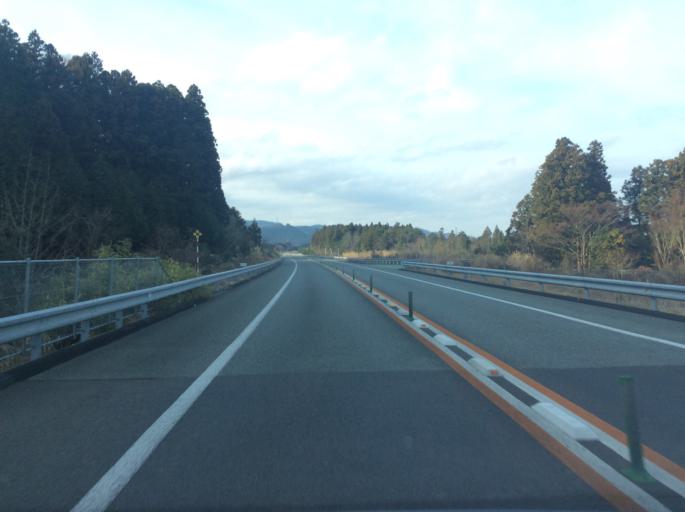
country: JP
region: Fukushima
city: Namie
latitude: 37.3488
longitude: 140.9848
